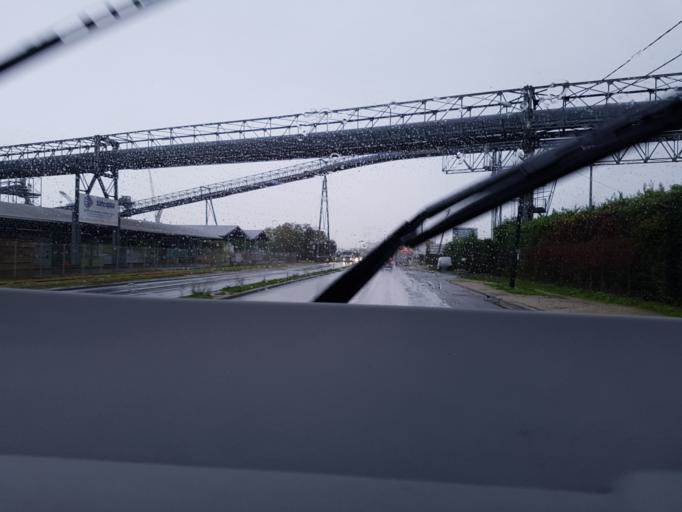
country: FR
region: Aquitaine
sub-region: Departement de la Gironde
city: Bassens
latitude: 44.8971
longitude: -0.5311
